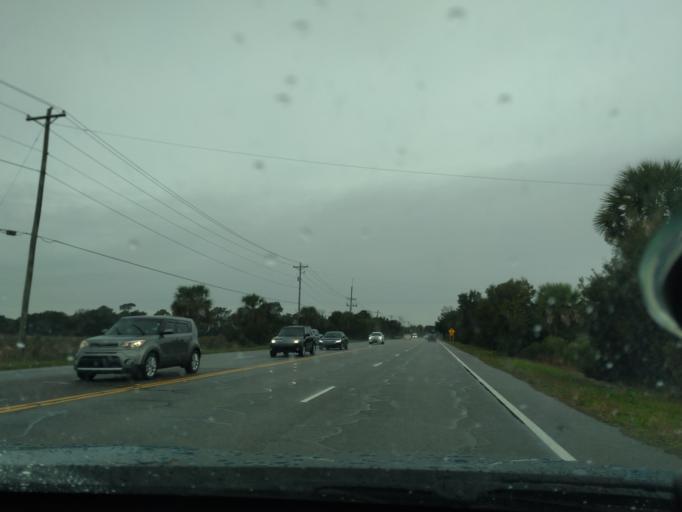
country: US
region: South Carolina
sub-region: Charleston County
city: Folly Beach
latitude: 32.6824
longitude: -79.9569
